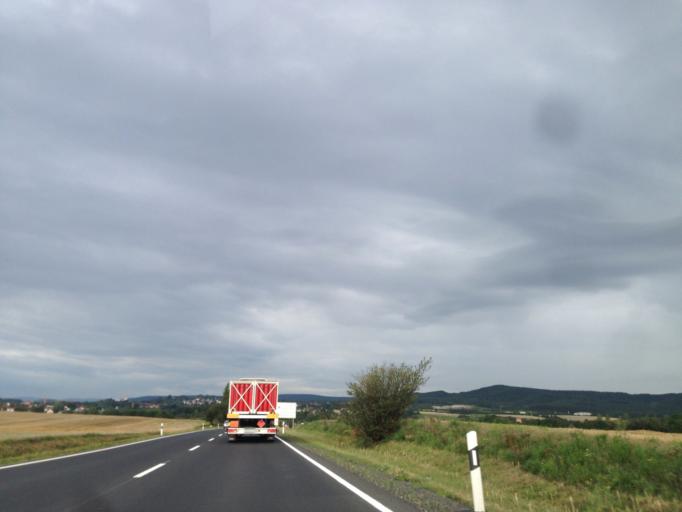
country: DE
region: Thuringia
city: Dobritz
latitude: 50.7050
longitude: 11.6322
